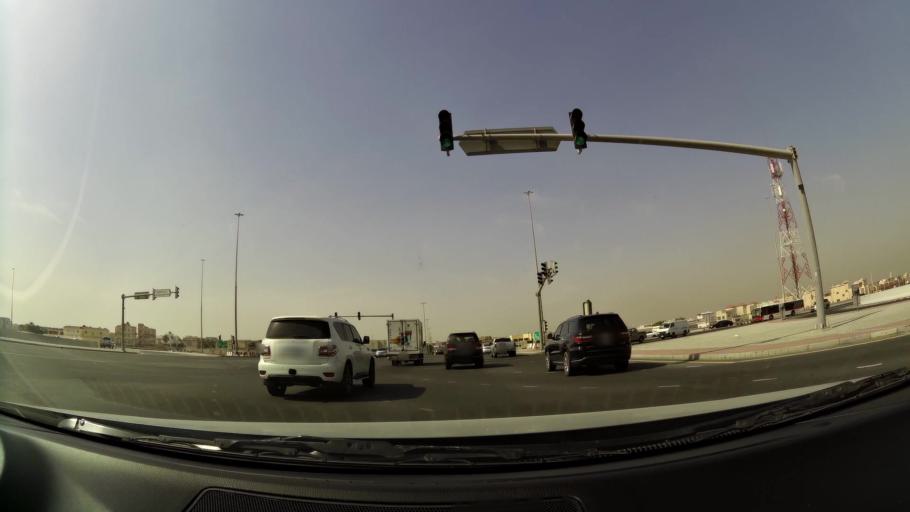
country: AE
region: Ash Shariqah
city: Sharjah
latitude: 25.2350
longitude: 55.4253
